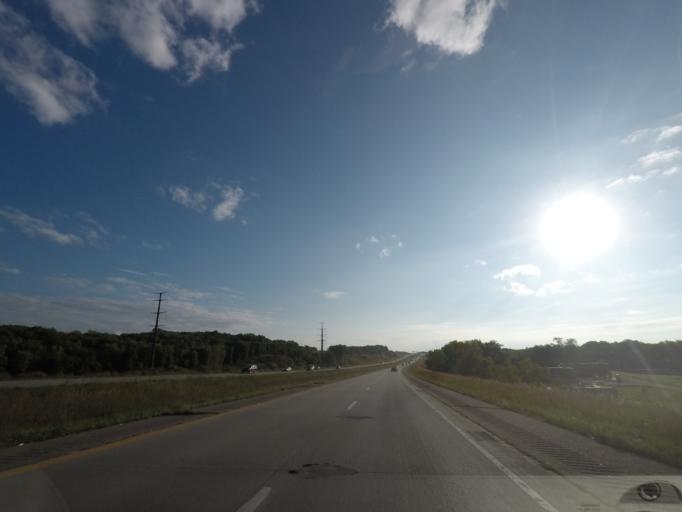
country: US
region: Iowa
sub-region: Warren County
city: Norwalk
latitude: 41.5029
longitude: -93.5911
